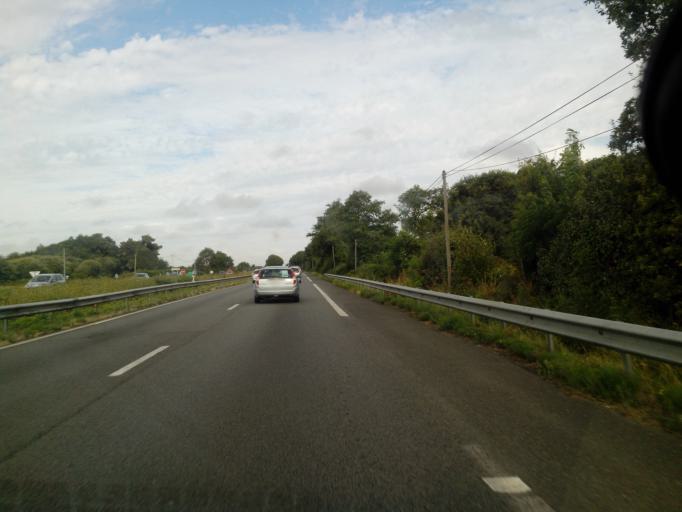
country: FR
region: Pays de la Loire
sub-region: Departement de la Loire-Atlantique
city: Le Temple-de-Bretagne
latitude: 47.3386
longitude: -1.8137
